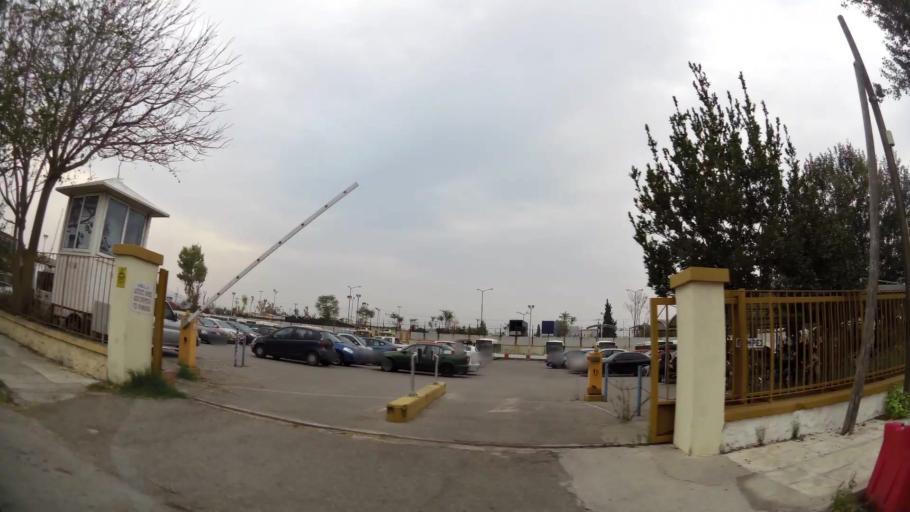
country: GR
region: Attica
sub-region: Nomos Piraios
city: Agios Ioannis Rentis
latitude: 37.9735
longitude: 23.6696
